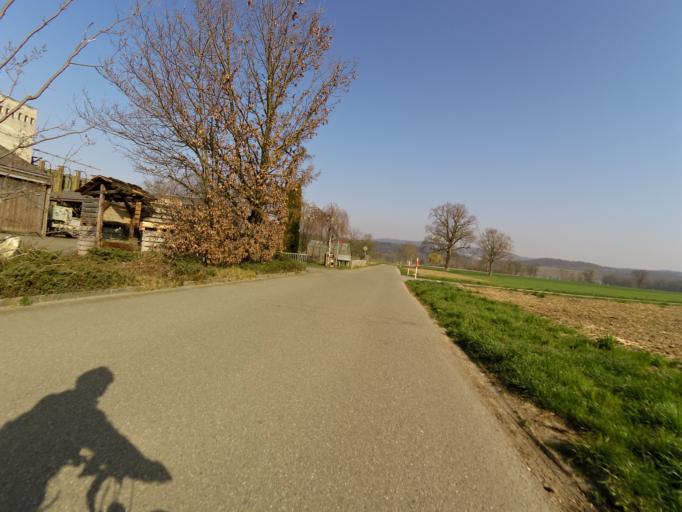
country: CH
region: Thurgau
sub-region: Frauenfeld District
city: Frauenfeld
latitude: 47.5742
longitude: 8.9133
